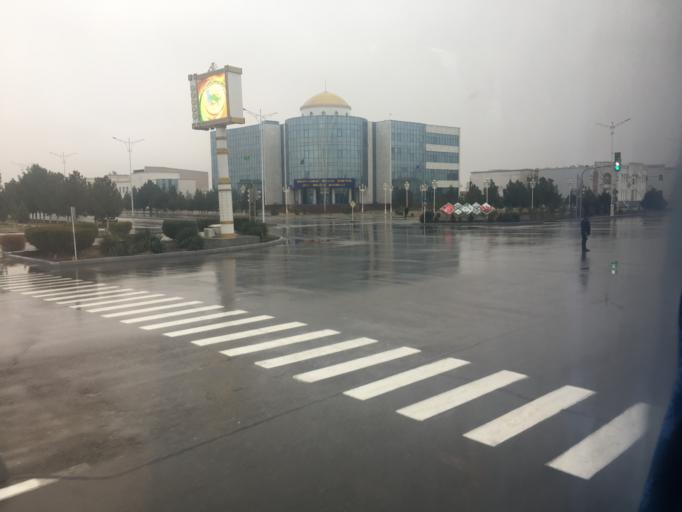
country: TM
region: Lebap
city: Turkmenabat
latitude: 39.0731
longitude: 63.5869
